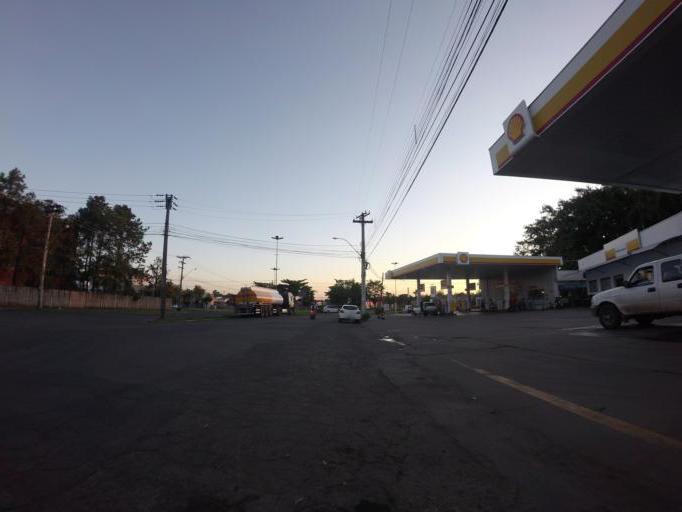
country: BR
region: Sao Paulo
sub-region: Piracicaba
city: Piracicaba
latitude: -22.7364
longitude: -47.5974
